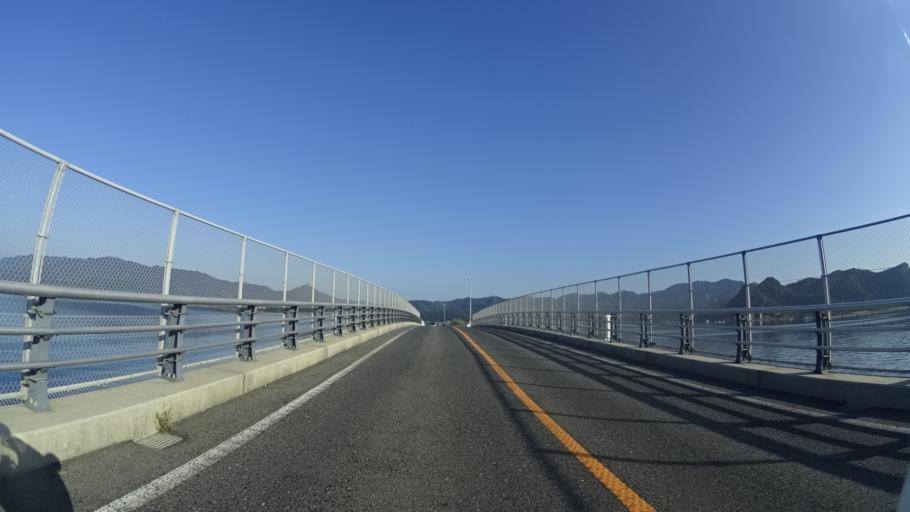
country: JP
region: Shimane
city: Sakaiminato
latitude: 35.5201
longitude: 133.1826
